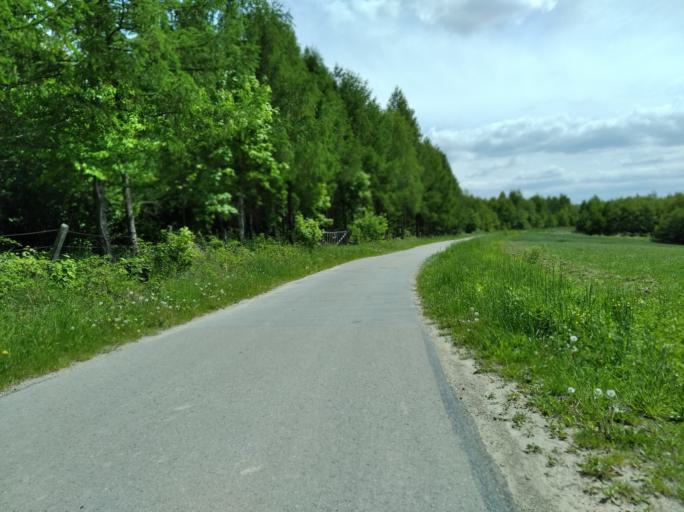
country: PL
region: Subcarpathian Voivodeship
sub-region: Powiat ropczycko-sedziszowski
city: Wielopole Skrzynskie
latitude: 49.9050
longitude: 21.6076
